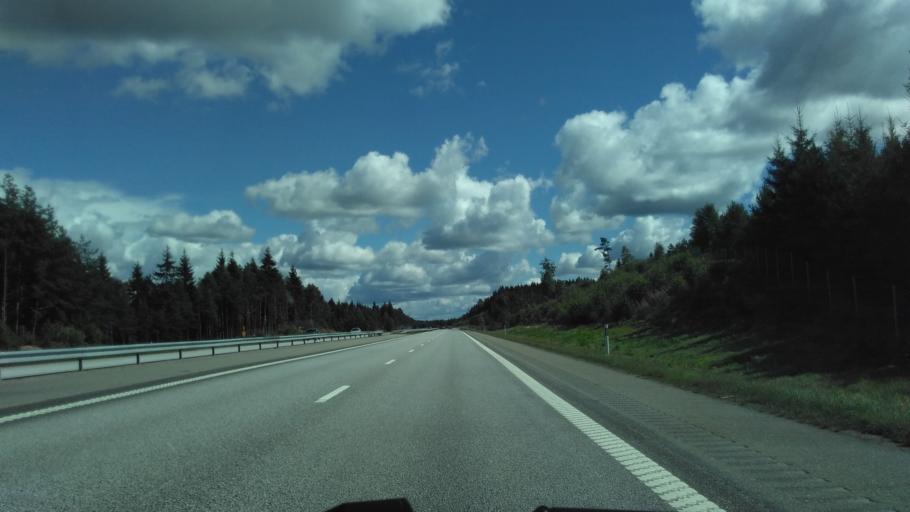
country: SE
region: Vaestra Goetaland
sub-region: Harryda Kommun
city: Hindas
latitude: 57.6720
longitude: 12.3648
